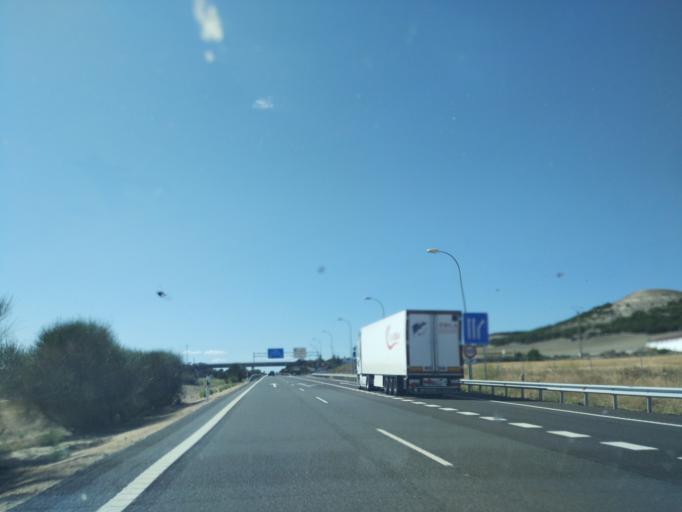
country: ES
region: Castille and Leon
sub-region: Provincia de Valladolid
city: Tordesillas
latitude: 41.5227
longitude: -5.0393
